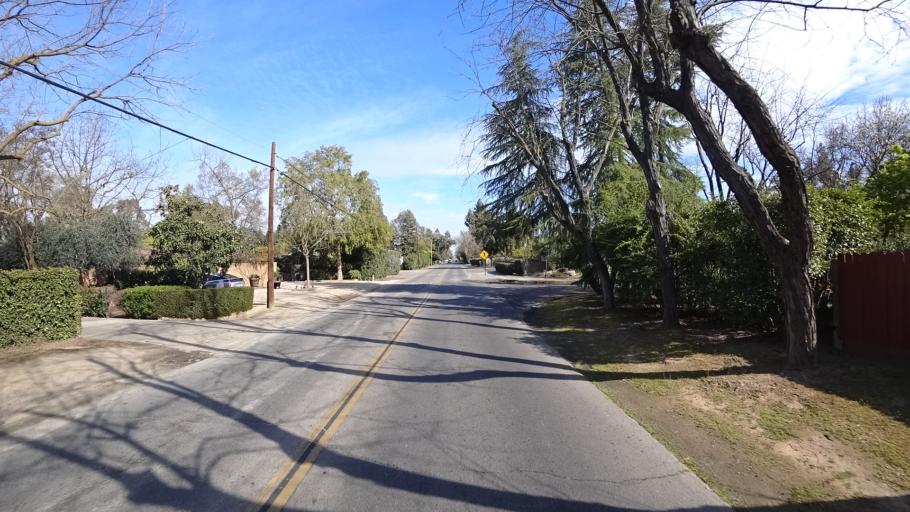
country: US
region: California
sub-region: Fresno County
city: Fresno
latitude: 36.8019
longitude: -119.7995
